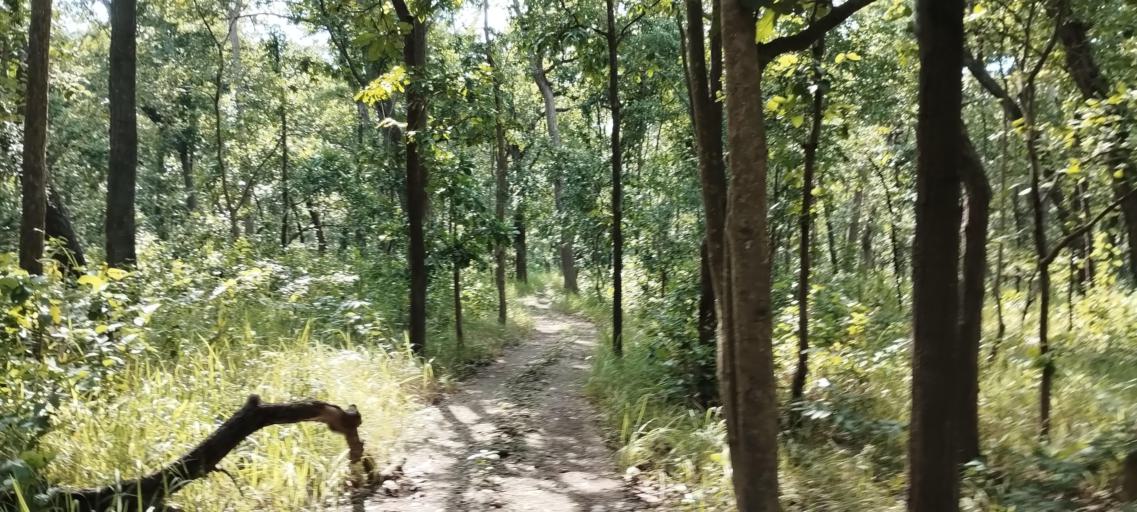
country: NP
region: Far Western
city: Tikapur
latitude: 28.5649
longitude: 81.2786
